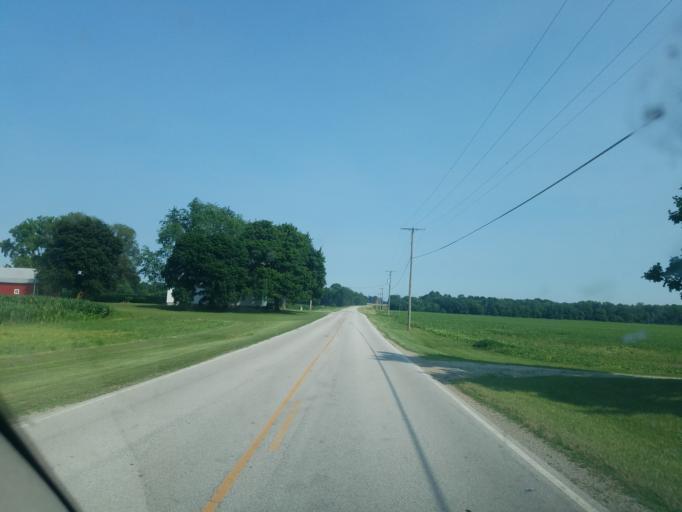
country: US
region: Ohio
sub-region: Wyandot County
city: Carey
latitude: 40.9833
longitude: -83.2471
